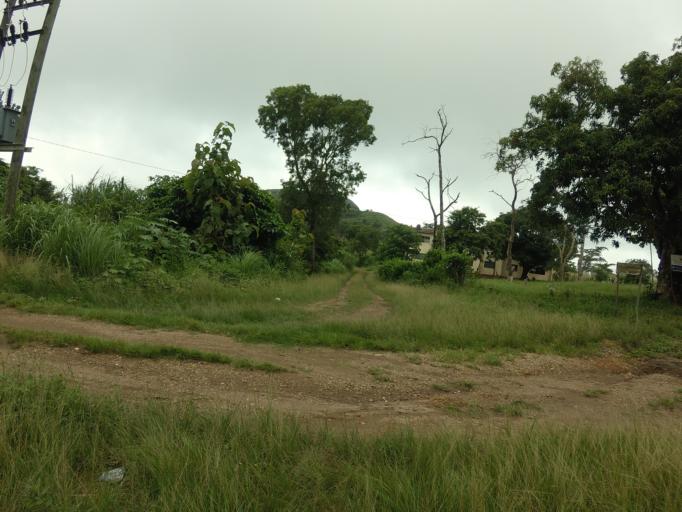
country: GH
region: Volta
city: Kpandu
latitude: 6.8510
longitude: 0.4352
